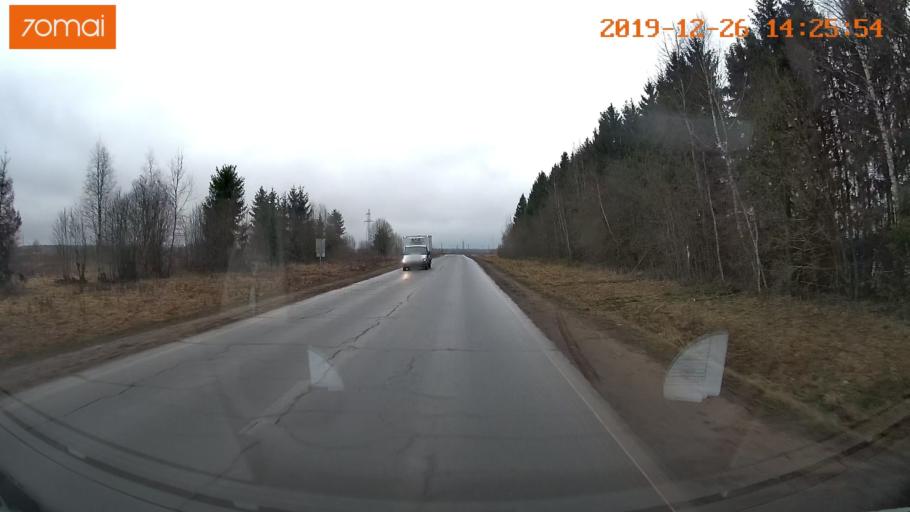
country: RU
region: Jaroslavl
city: Poshekhon'ye
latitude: 58.4904
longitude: 39.0909
